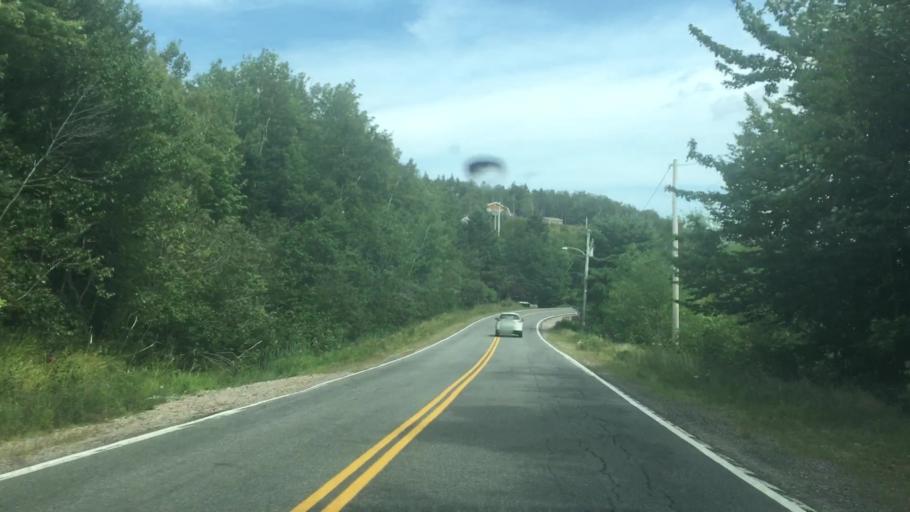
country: CA
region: Nova Scotia
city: Sydney Mines
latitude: 46.6356
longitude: -60.4214
